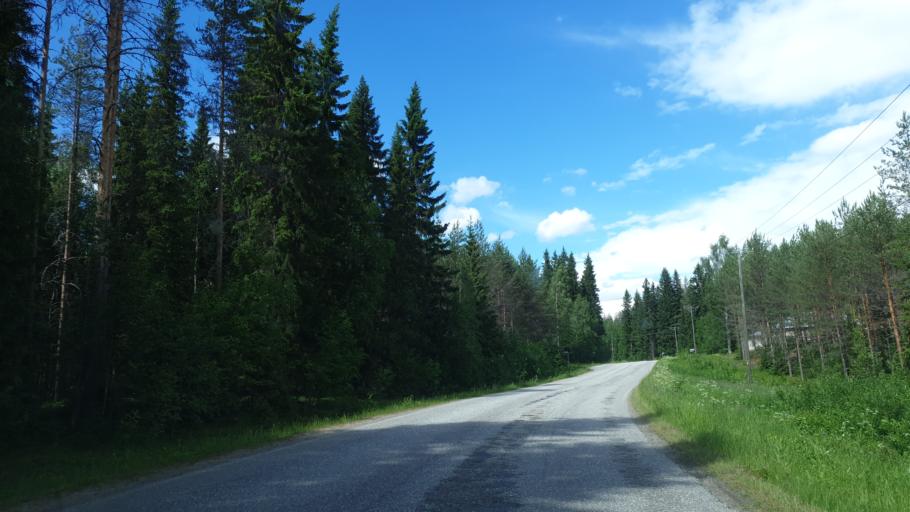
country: FI
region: Northern Savo
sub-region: Koillis-Savo
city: Kaavi
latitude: 63.0161
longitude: 28.6525
